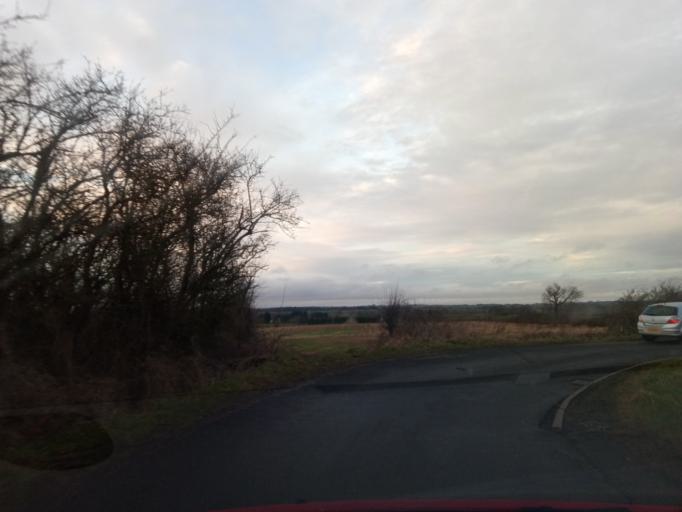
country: GB
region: England
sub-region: Northumberland
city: Ponteland
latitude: 55.0800
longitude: -1.7390
